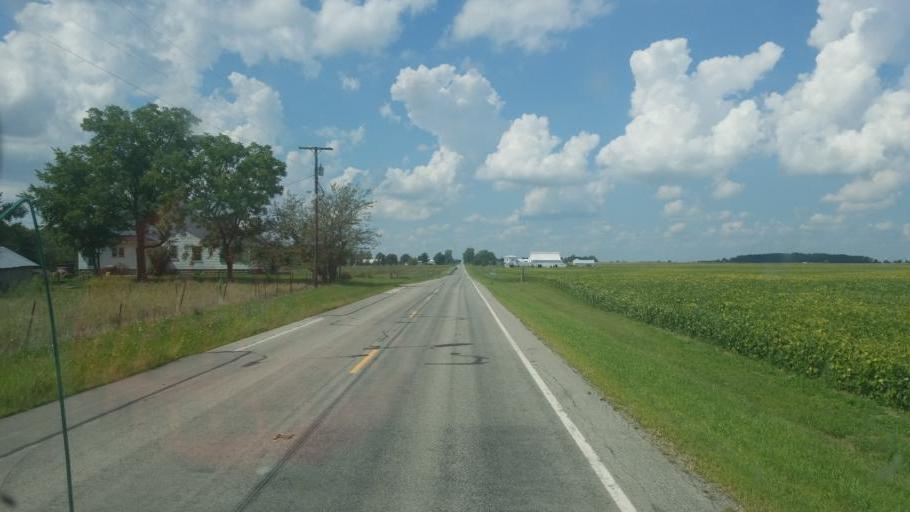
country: US
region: Ohio
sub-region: Hardin County
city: Kenton
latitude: 40.7320
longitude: -83.6535
